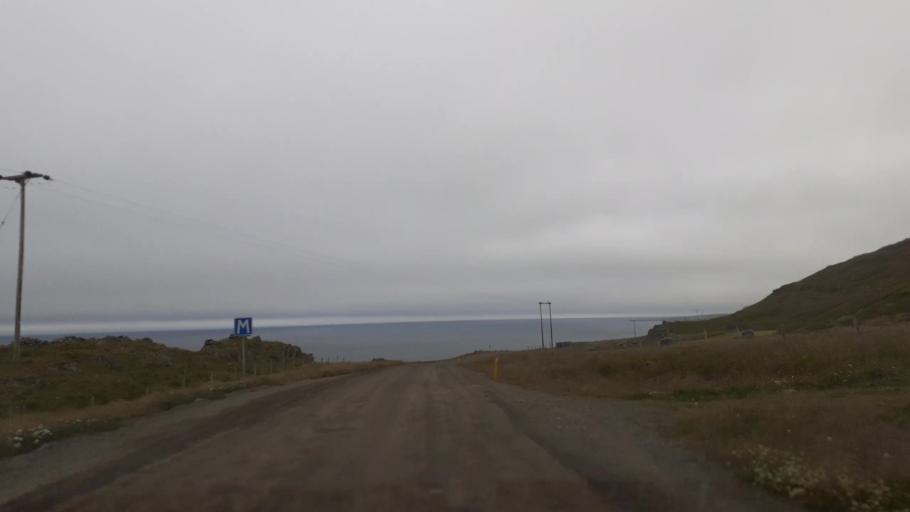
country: IS
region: Northwest
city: Saudarkrokur
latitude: 65.5131
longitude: -20.9714
